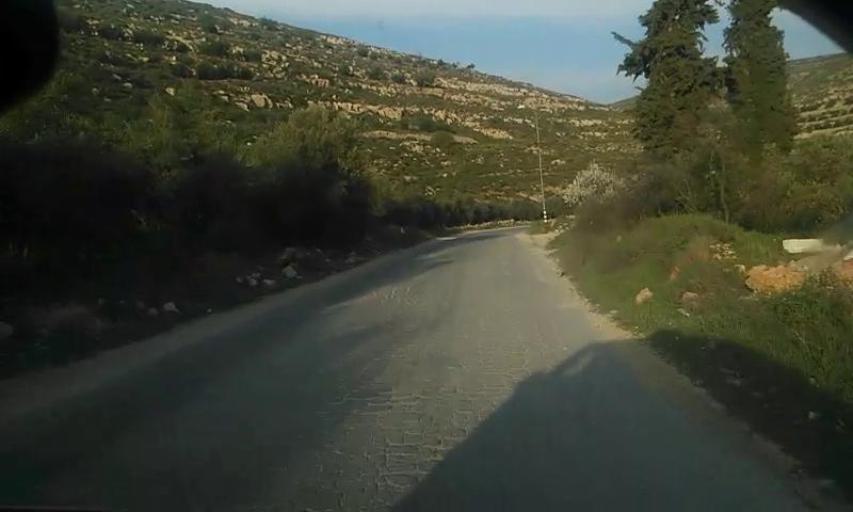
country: PS
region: West Bank
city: Marah Rabbah
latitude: 31.5991
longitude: 35.1820
